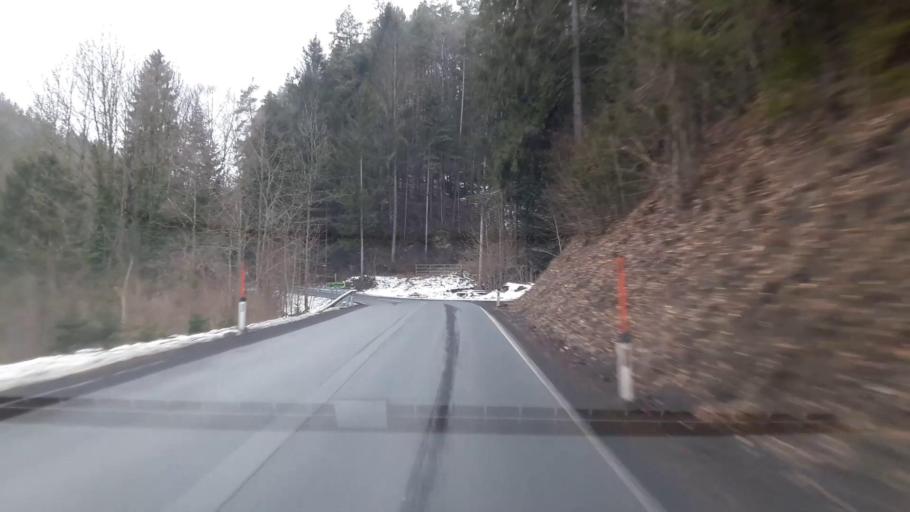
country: AT
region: Lower Austria
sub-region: Politischer Bezirk Neunkirchen
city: Feistritz am Wechsel
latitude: 47.5559
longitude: 16.0721
